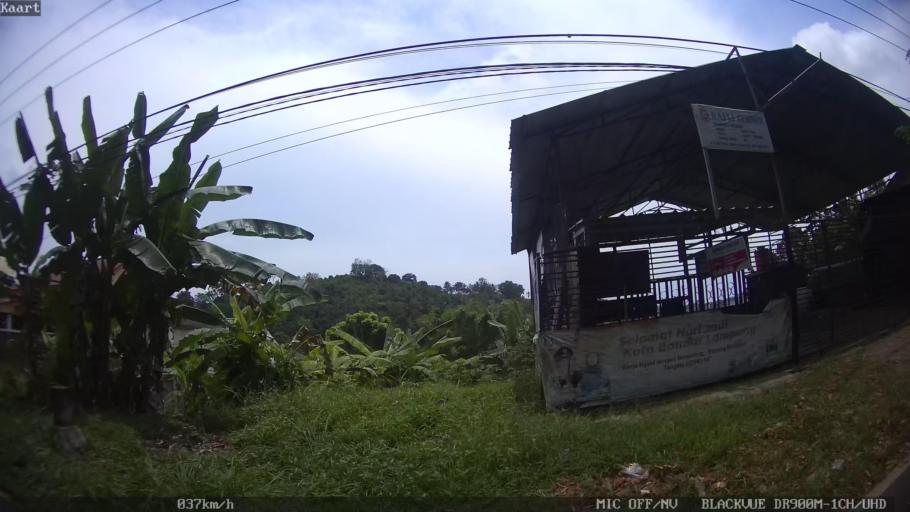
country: ID
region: Lampung
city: Bandarlampung
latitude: -5.4129
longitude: 105.2356
